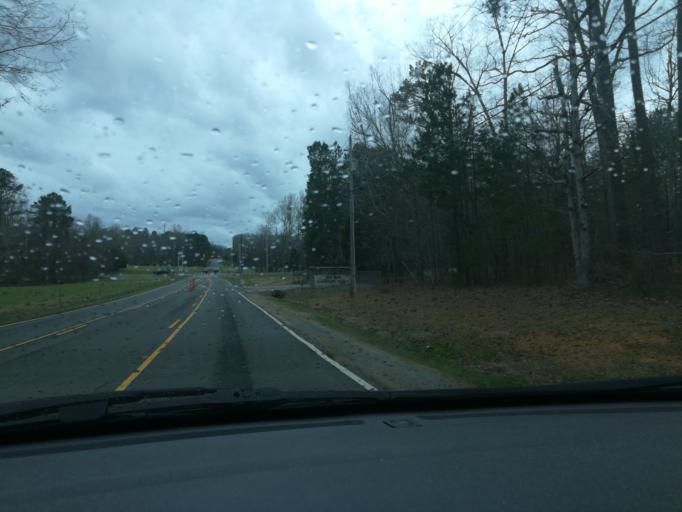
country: US
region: North Carolina
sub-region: Orange County
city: Hillsborough
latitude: 36.0186
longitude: -79.0744
